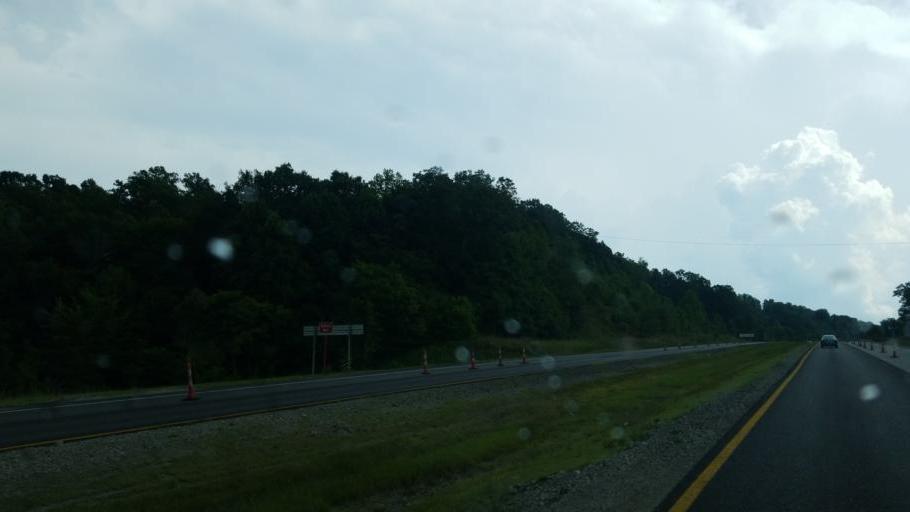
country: US
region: West Virginia
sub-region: Kanawha County
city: Alum Creek
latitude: 38.2504
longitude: -81.8369
